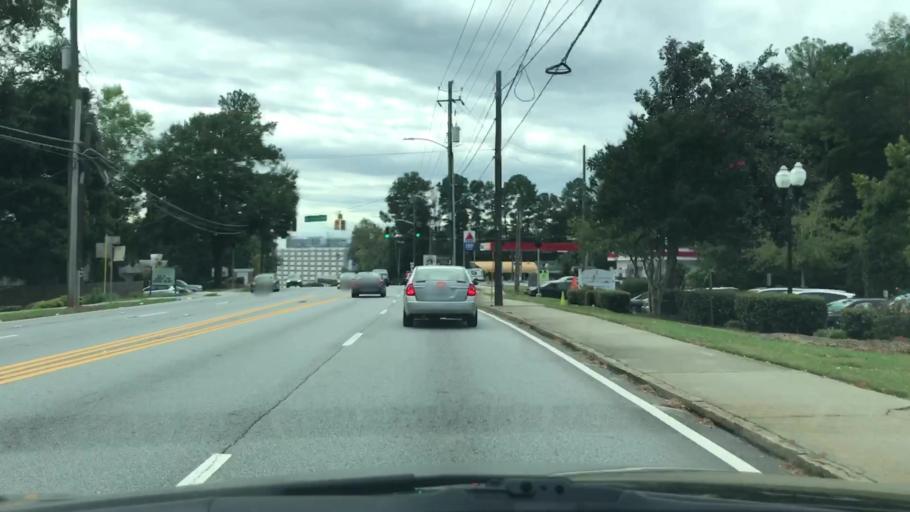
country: US
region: Georgia
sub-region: DeKalb County
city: North Druid Hills
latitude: 33.8076
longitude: -84.3102
